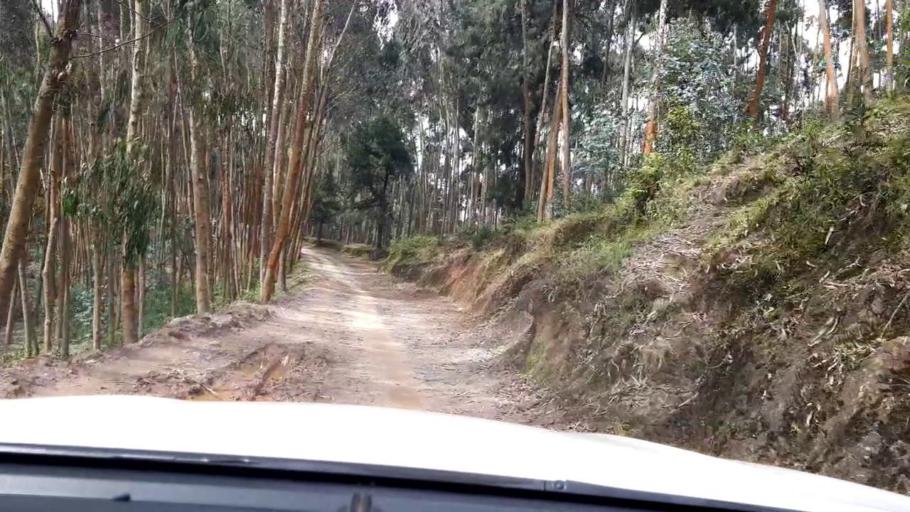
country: RW
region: Western Province
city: Kibuye
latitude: -1.8716
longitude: 29.4511
